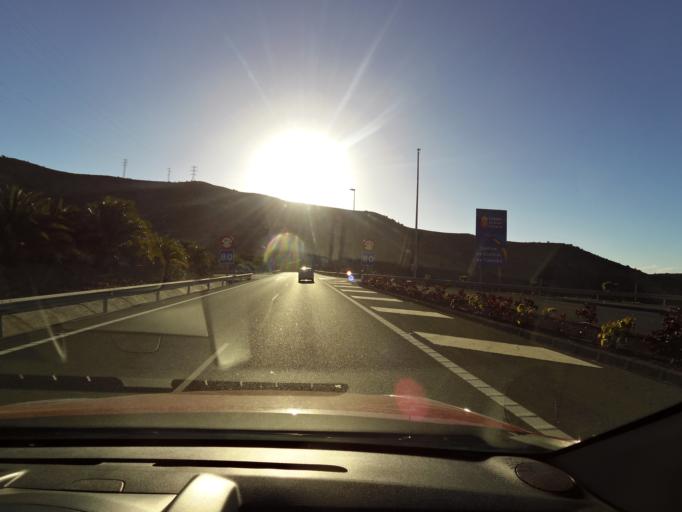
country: ES
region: Canary Islands
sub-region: Provincia de Las Palmas
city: Puerto Rico
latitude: 27.7881
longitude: -15.6925
